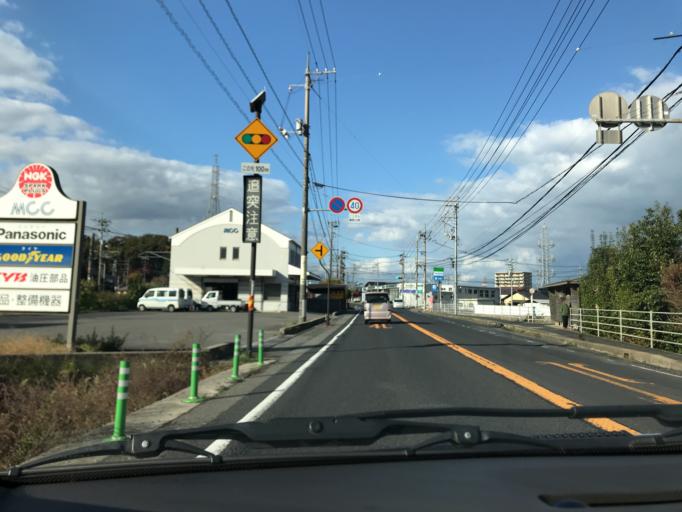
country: JP
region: Shimane
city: Yasugicho
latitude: 35.4284
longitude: 133.2663
